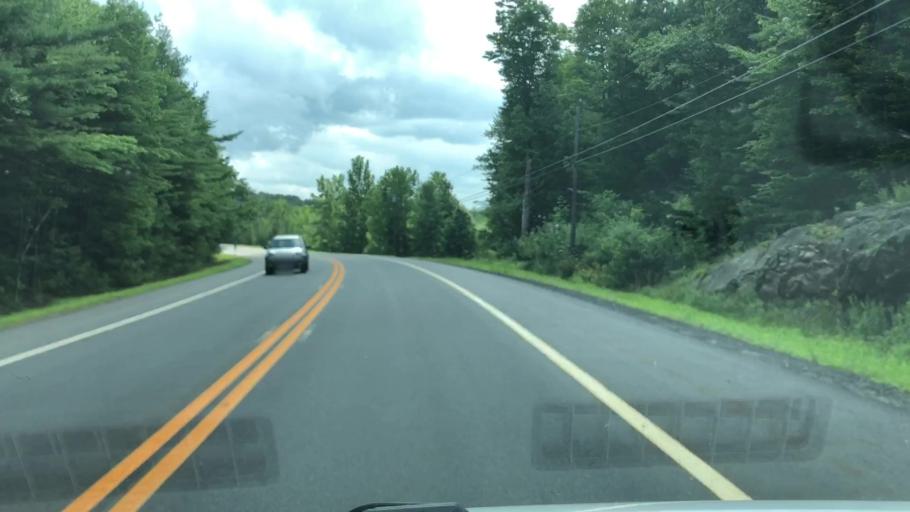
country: US
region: Massachusetts
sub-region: Franklin County
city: Ashfield
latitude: 42.5042
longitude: -72.8115
